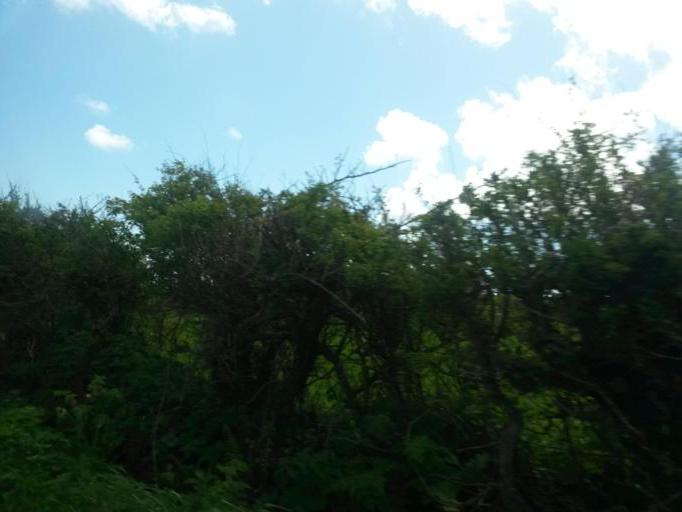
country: IE
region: Munster
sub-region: Waterford
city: Dunmore East
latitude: 52.1910
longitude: -6.8981
